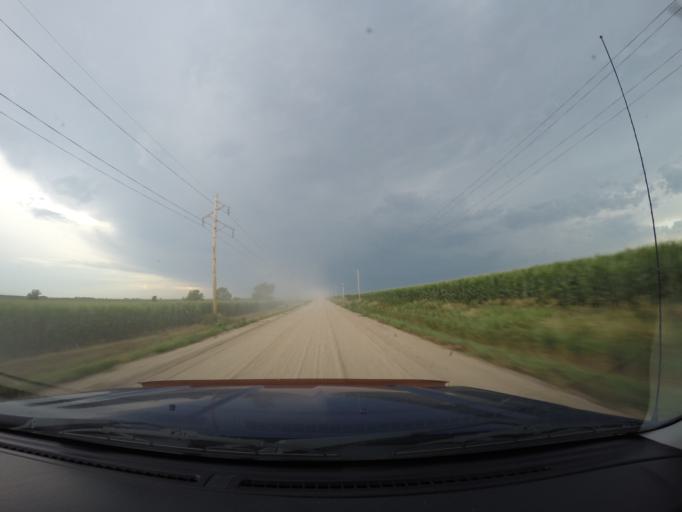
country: US
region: Nebraska
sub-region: Buffalo County
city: Kearney
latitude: 40.8438
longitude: -99.1780
